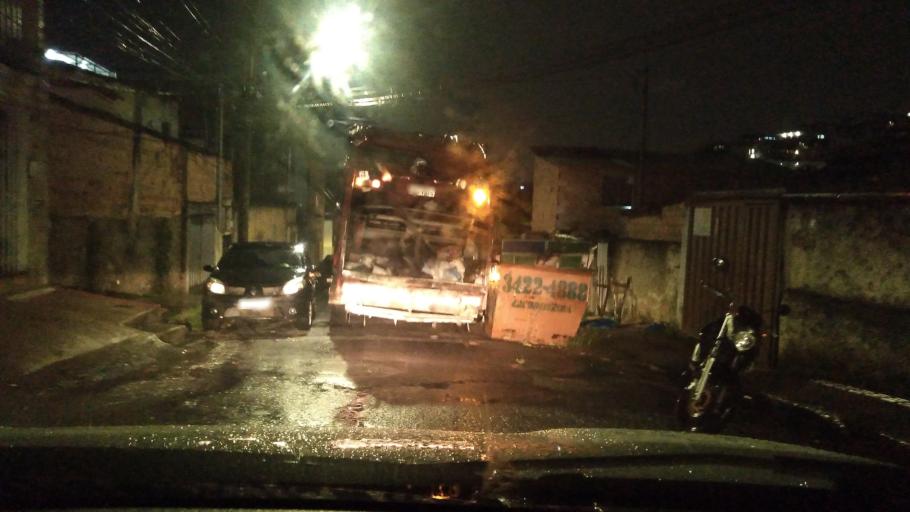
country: BR
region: Minas Gerais
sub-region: Belo Horizonte
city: Belo Horizonte
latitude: -19.8982
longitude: -43.9583
